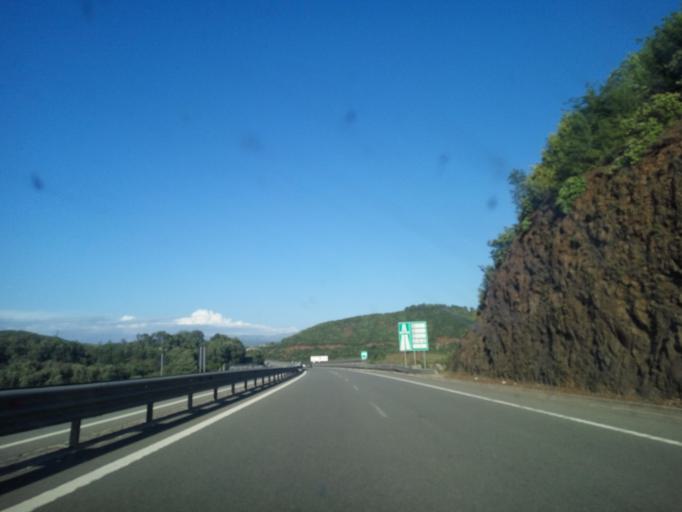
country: AL
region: Lezhe
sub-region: Rrethi i Mirdites
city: Rreshen
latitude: 41.7808
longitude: 19.8492
